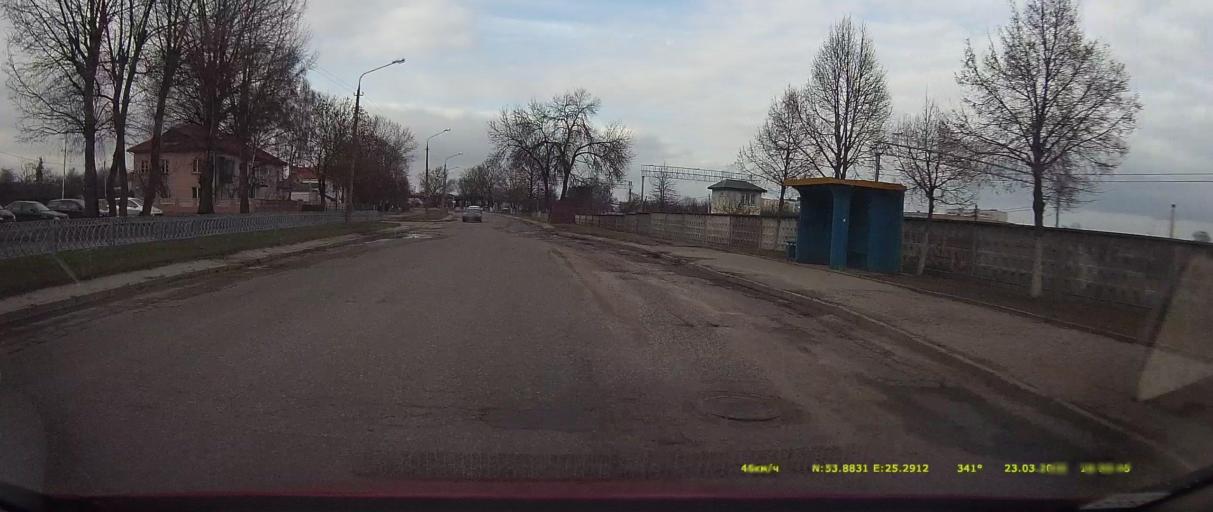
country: BY
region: Grodnenskaya
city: Lida
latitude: 53.8832
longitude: 25.2912
